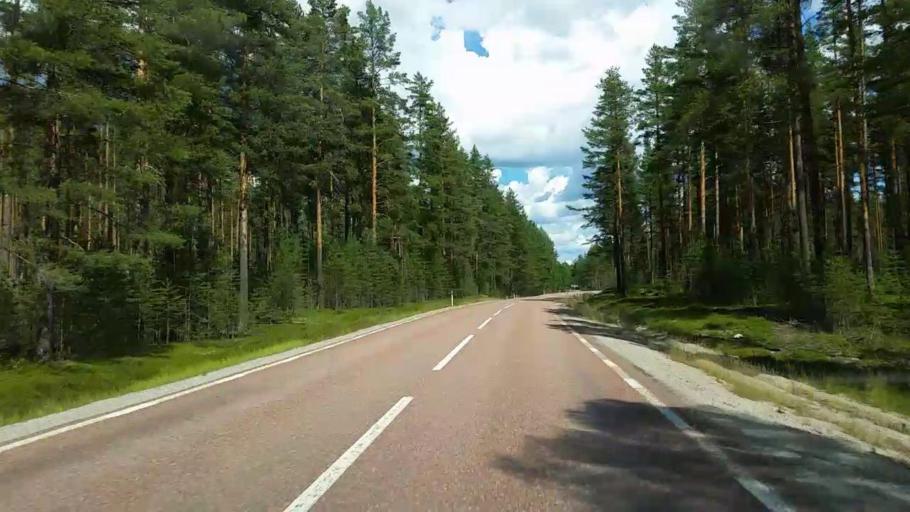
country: SE
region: Gaevleborg
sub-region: Ovanakers Kommun
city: Edsbyn
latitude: 61.3501
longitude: 15.5754
